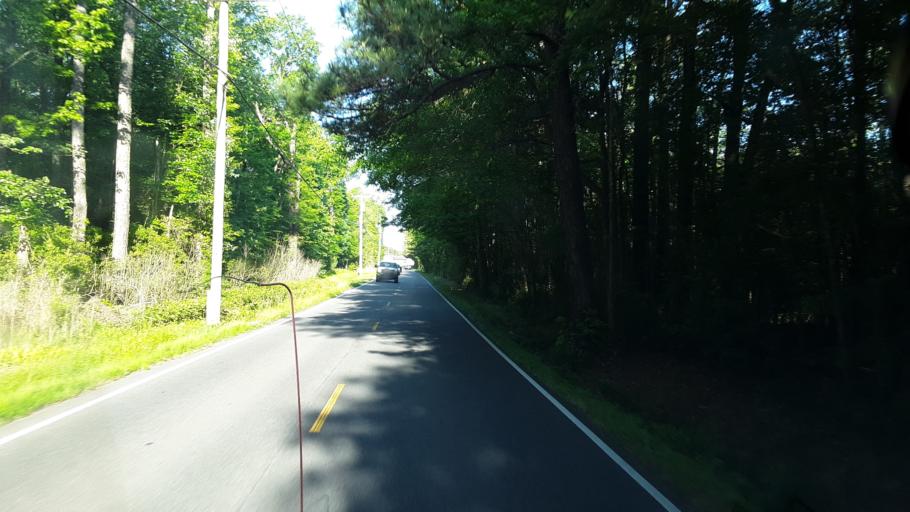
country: US
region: Virginia
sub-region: City of Virginia Beach
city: Virginia Beach
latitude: 36.7205
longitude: -76.0398
